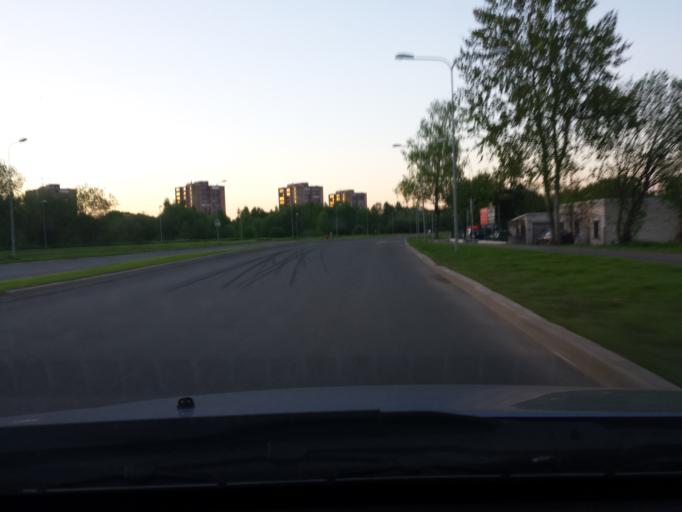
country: LV
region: Riga
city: Jaunciems
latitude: 56.9911
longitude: 24.1667
